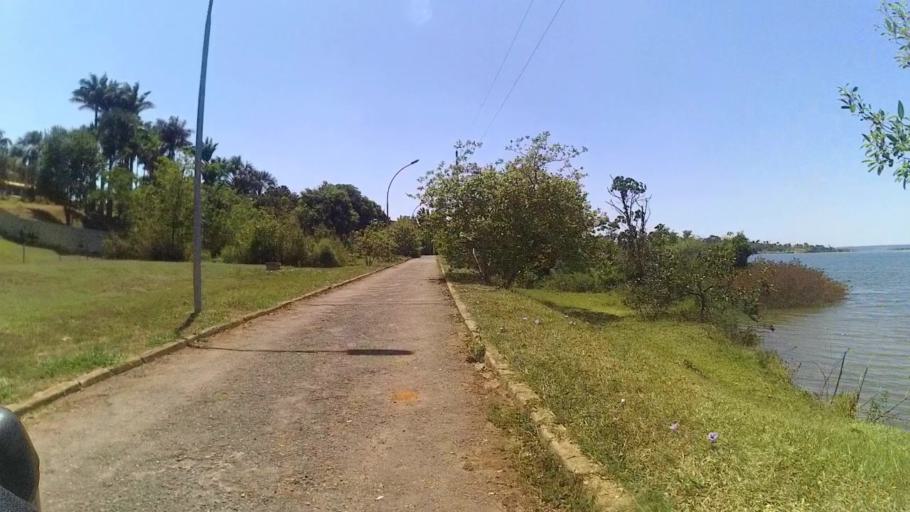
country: BR
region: Federal District
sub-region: Brasilia
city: Brasilia
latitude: -15.7291
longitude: -47.8868
